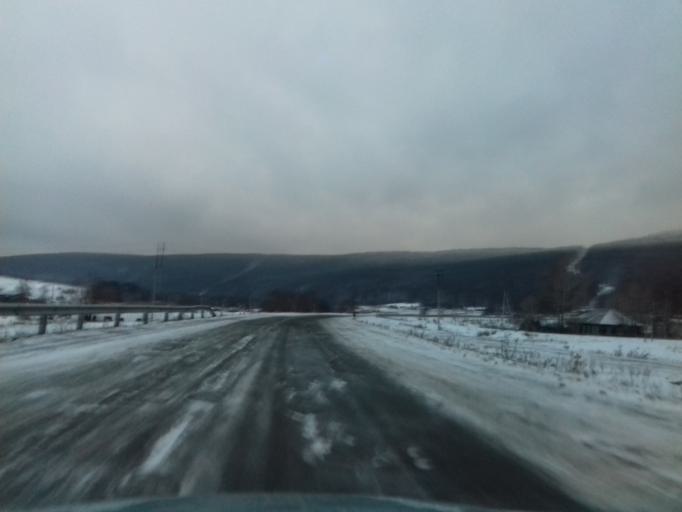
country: RU
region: Bashkortostan
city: Verkhniy Avzyan
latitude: 53.6963
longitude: 57.8506
